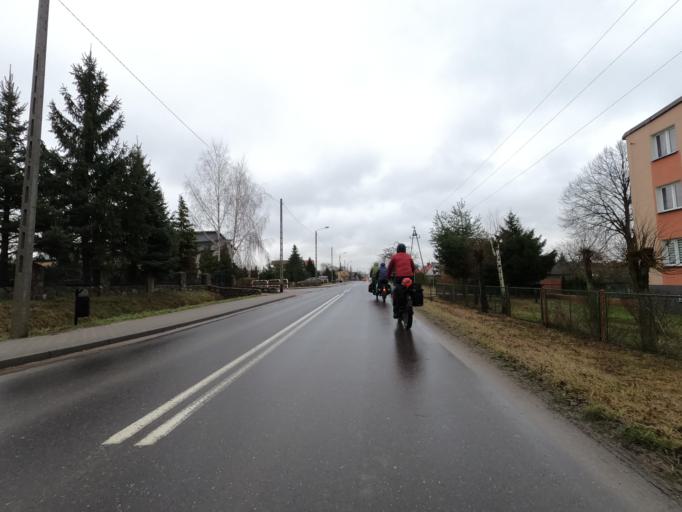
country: PL
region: Greater Poland Voivodeship
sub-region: Powiat pilski
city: Osiek nad Notecia
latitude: 53.1209
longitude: 17.2855
